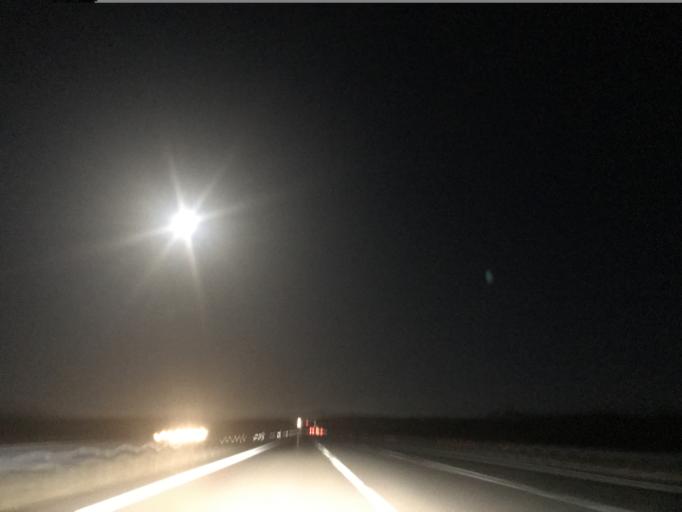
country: TR
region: Nigde
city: Ulukisla
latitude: 37.6388
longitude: 34.3918
